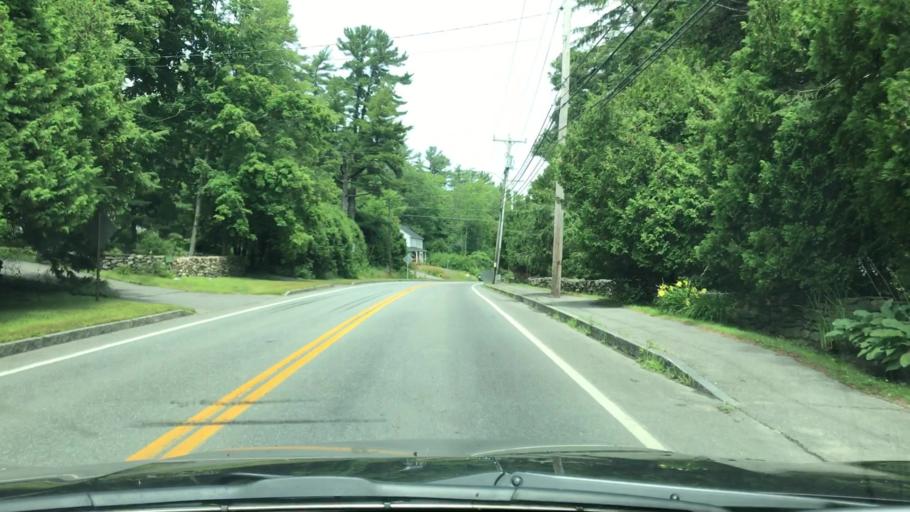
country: US
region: Maine
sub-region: Knox County
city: Camden
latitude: 44.2192
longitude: -69.0559
